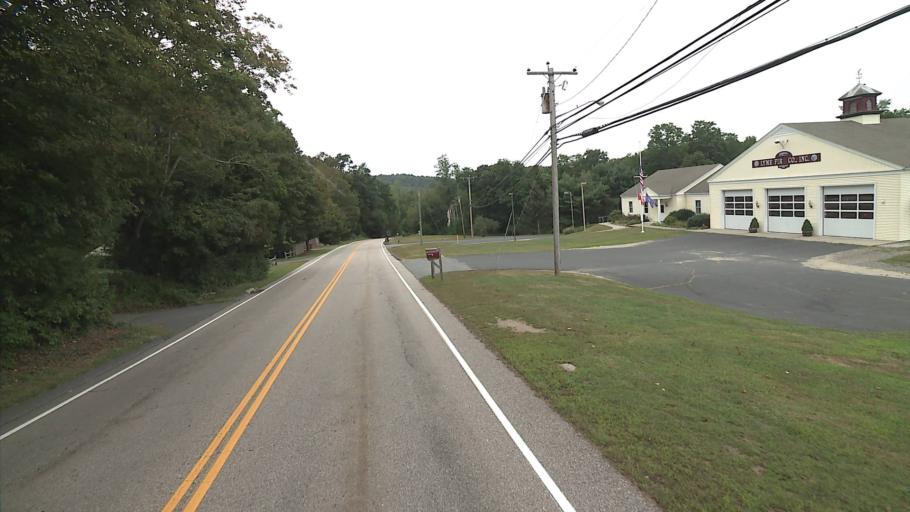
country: US
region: Connecticut
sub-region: Middlesex County
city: Essex Village
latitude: 41.3805
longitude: -72.3497
